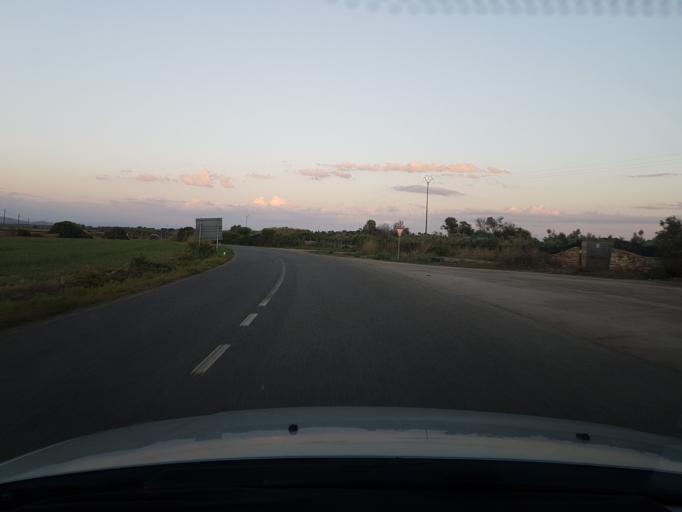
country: IT
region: Sardinia
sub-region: Provincia di Oristano
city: Riola Sardo
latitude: 40.0253
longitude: 8.4311
